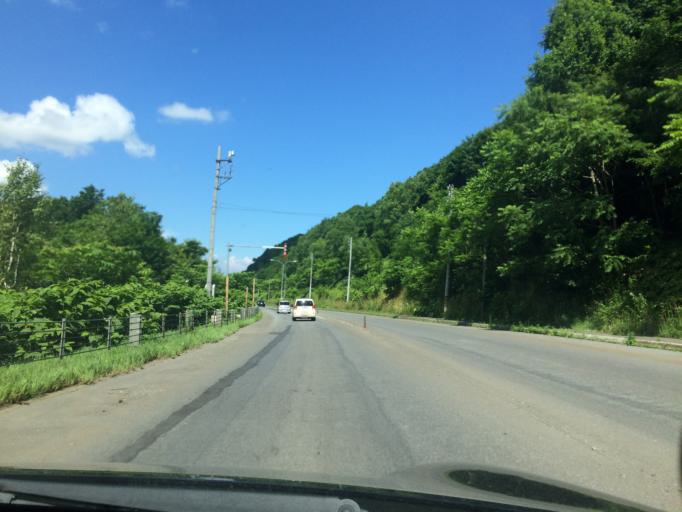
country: JP
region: Hokkaido
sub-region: Asahikawa-shi
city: Asahikawa
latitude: 43.7548
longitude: 142.2734
